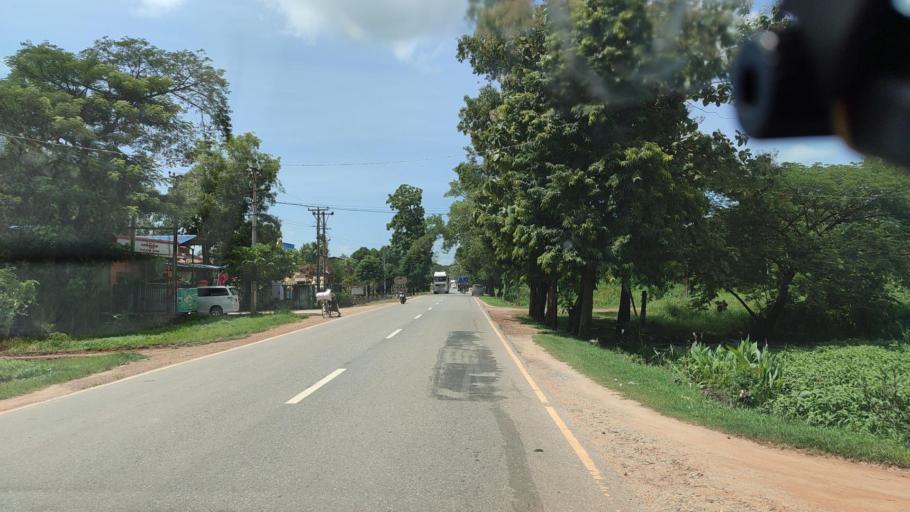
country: MM
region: Bago
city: Paungde
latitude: 18.2181
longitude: 95.6508
